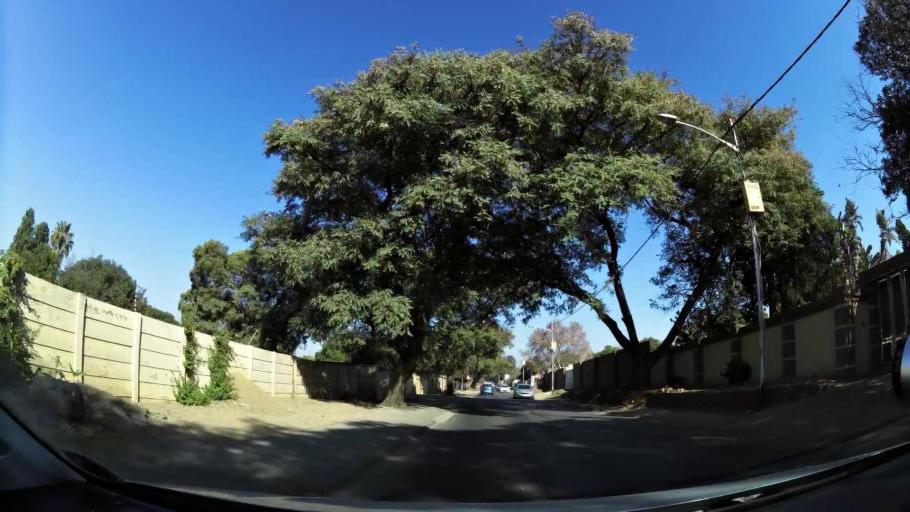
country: ZA
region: Gauteng
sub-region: City of Johannesburg Metropolitan Municipality
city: Modderfontein
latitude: -26.1207
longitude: 28.0936
